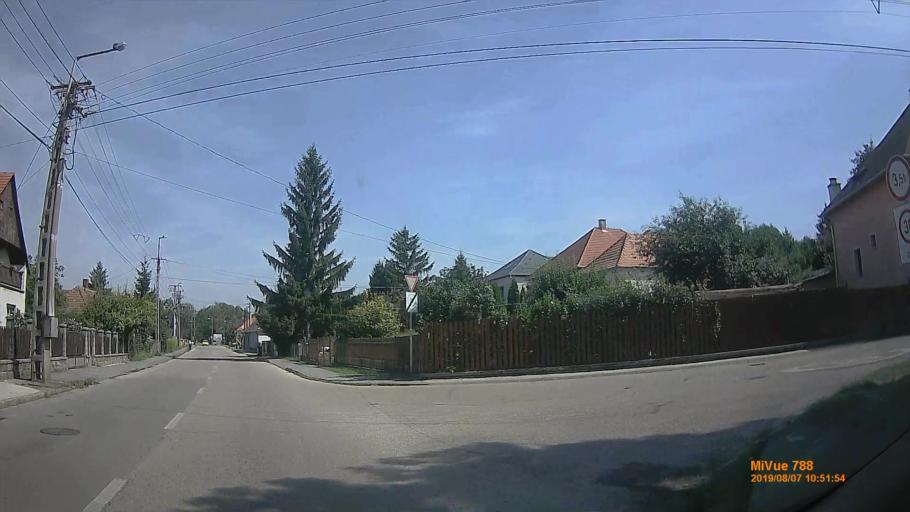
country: HU
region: Veszprem
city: Ajka
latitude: 47.0904
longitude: 17.5639
